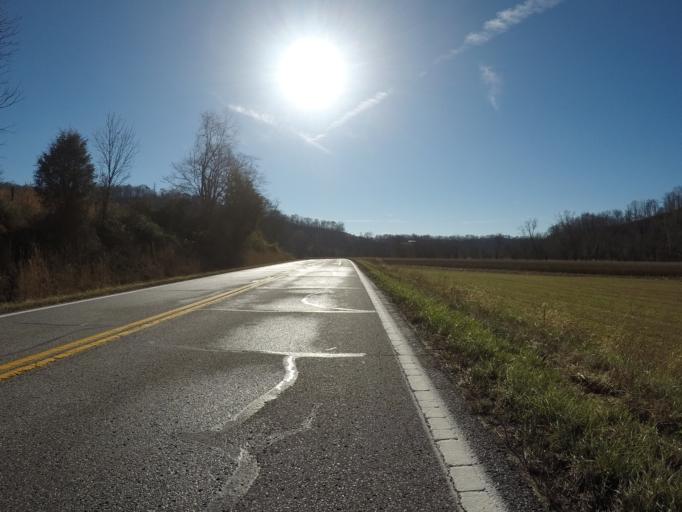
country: US
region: West Virginia
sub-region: Cabell County
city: Huntington
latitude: 38.4791
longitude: -82.4459
